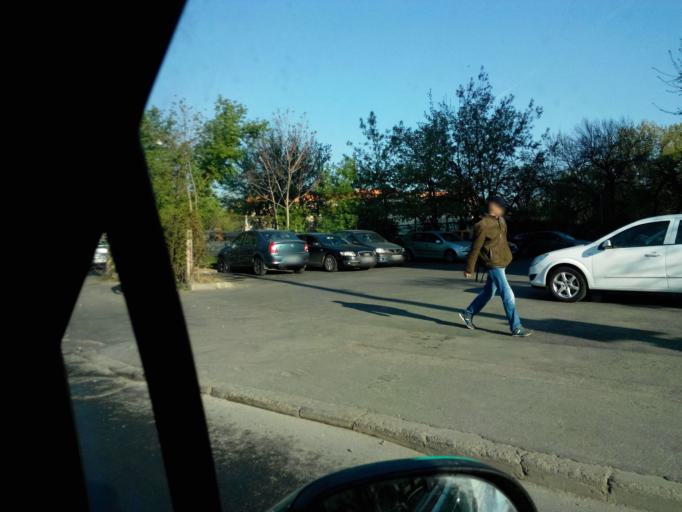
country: RO
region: Ilfov
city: Dobroesti
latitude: 44.4374
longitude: 26.1708
